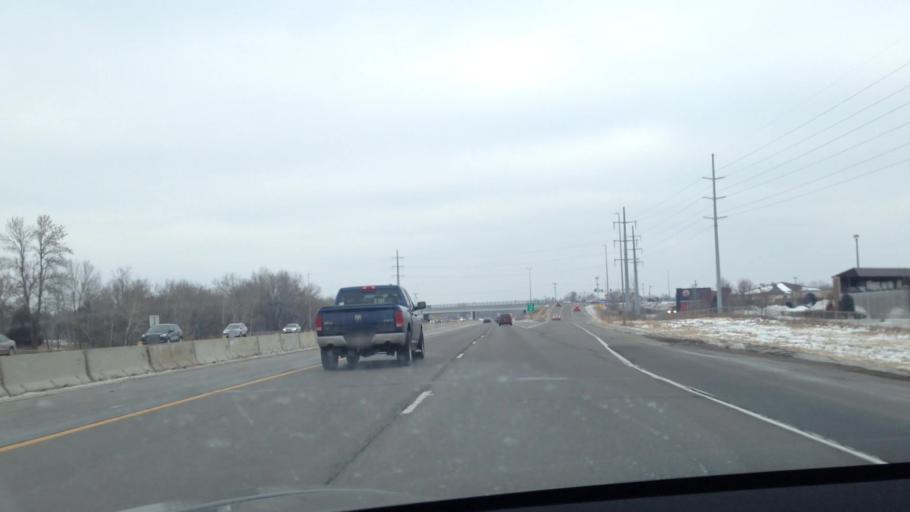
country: US
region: Minnesota
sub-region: Anoka County
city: Lexington
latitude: 45.1558
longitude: -93.1682
